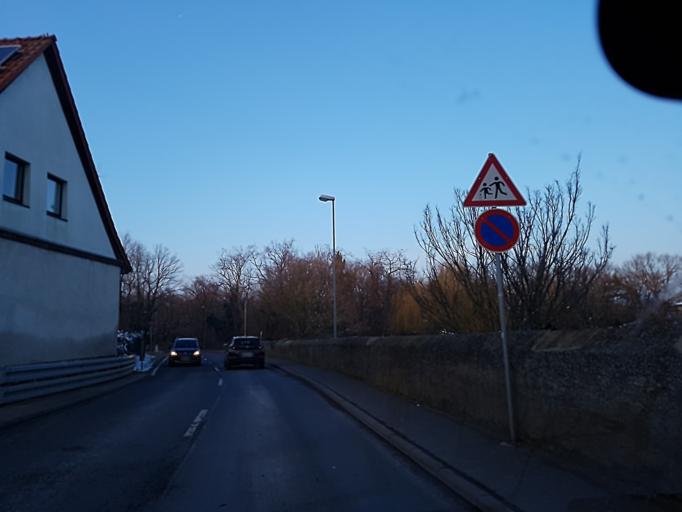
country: DE
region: Saxony
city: Strehla
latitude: 51.3549
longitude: 13.2241
